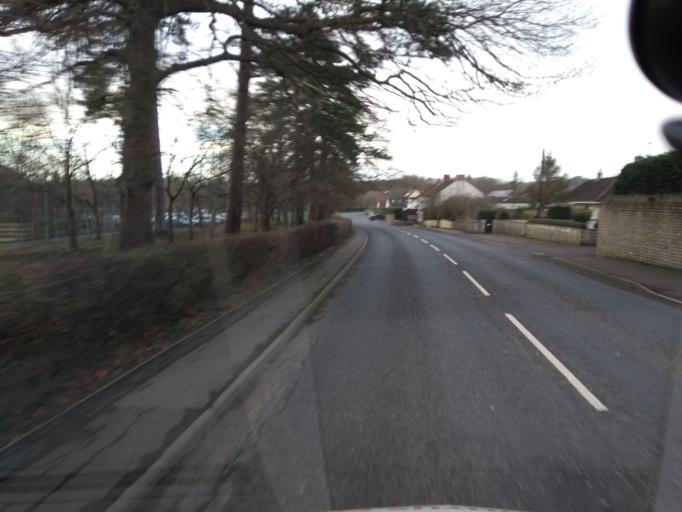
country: GB
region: England
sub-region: Somerset
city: Street
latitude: 51.1217
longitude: -2.7312
